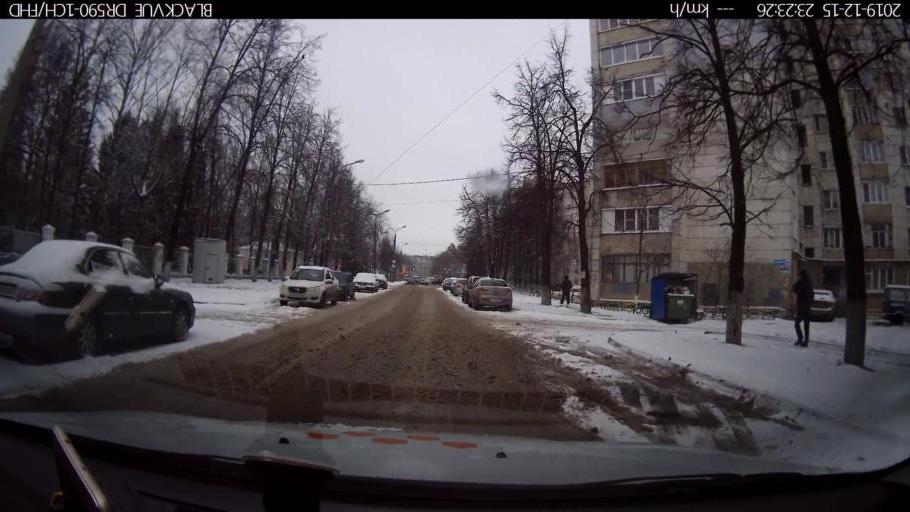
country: RU
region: Nizjnij Novgorod
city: Nizhniy Novgorod
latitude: 56.3175
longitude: 43.8723
